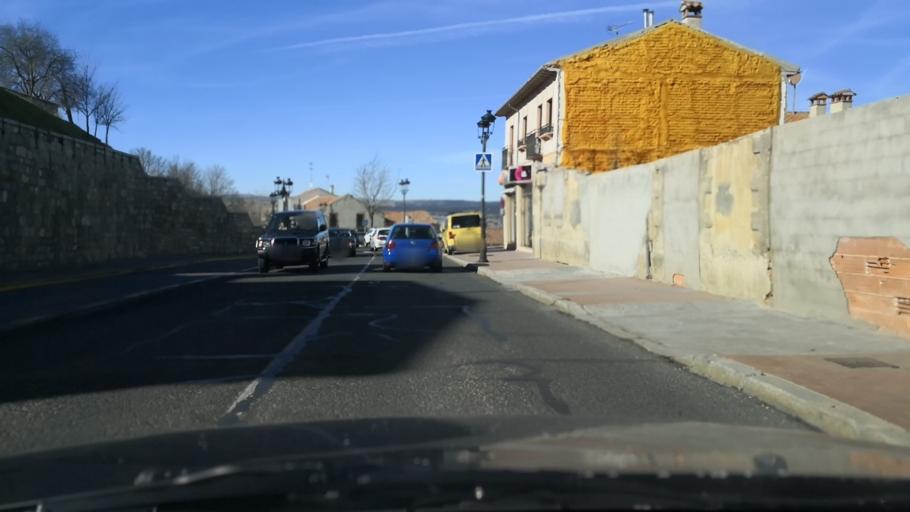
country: ES
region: Castille and Leon
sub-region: Provincia de Avila
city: Avila
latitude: 40.6586
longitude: -4.6968
